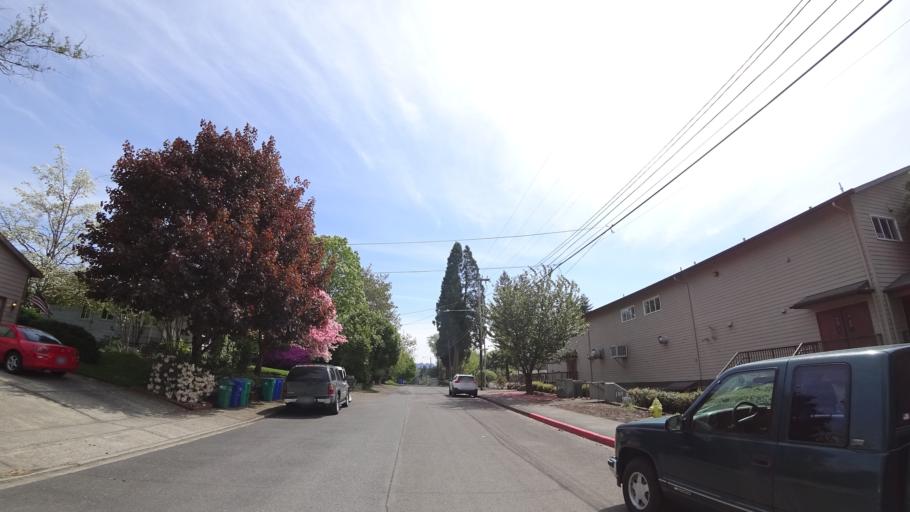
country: US
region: Oregon
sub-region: Clackamas County
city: Milwaukie
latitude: 45.4459
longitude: -122.6187
